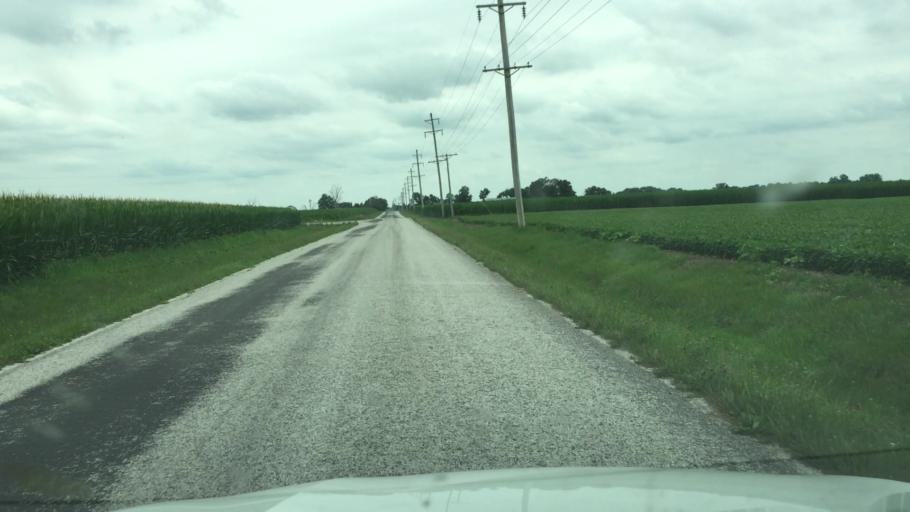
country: US
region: Illinois
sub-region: Hancock County
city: Carthage
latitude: 40.3945
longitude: -91.0826
